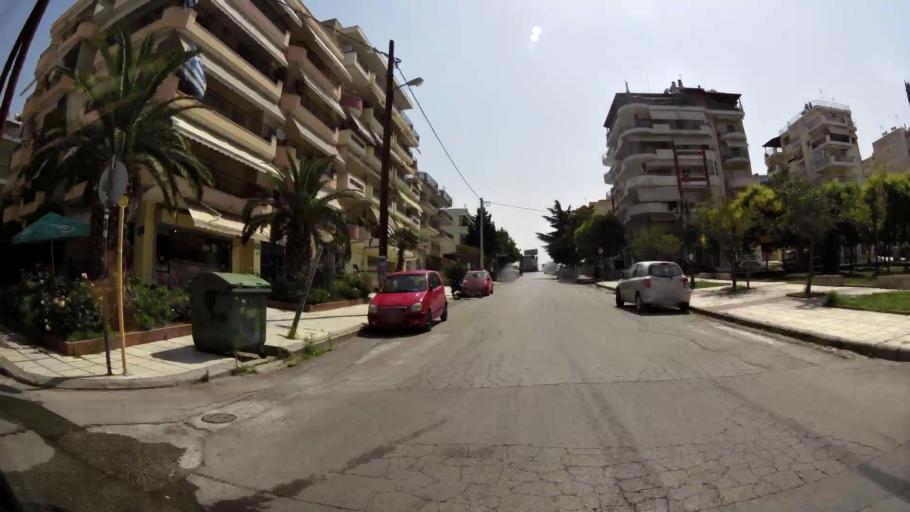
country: GR
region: Central Macedonia
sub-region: Nomos Thessalonikis
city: Evosmos
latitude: 40.6727
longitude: 22.9222
